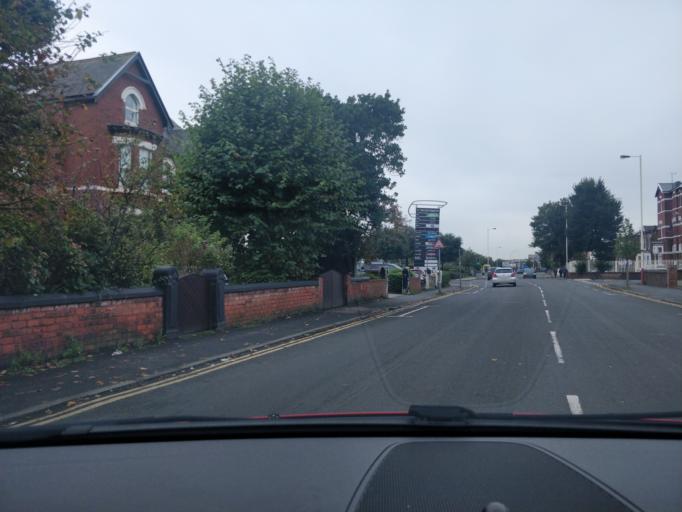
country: GB
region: England
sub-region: Sefton
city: Southport
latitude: 53.6472
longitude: -2.9957
